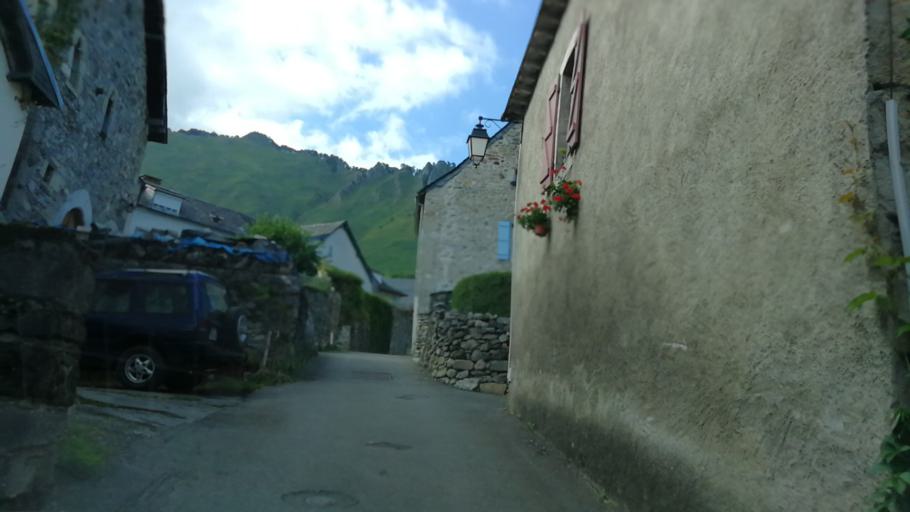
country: FR
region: Aquitaine
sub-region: Departement des Pyrenees-Atlantiques
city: Arette
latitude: 42.9331
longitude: -0.6347
